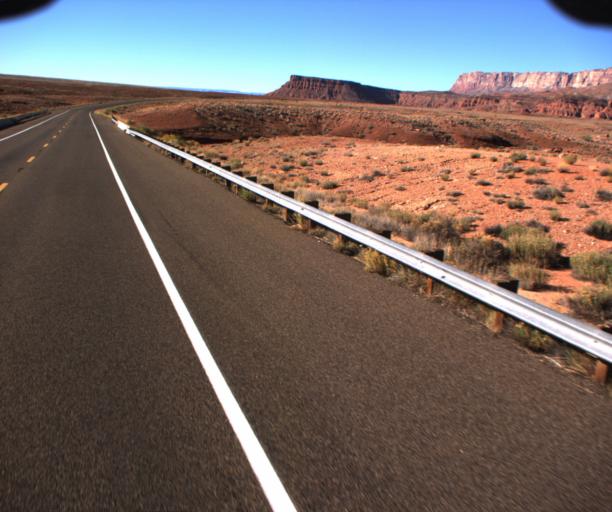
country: US
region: Arizona
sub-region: Coconino County
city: Page
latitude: 36.7837
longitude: -111.6875
